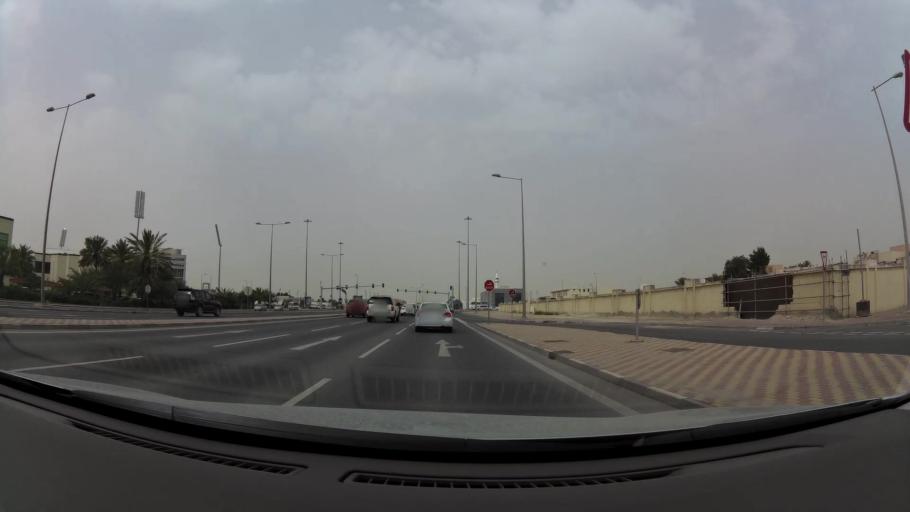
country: QA
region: Baladiyat ad Dawhah
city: Doha
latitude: 25.2544
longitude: 51.5379
